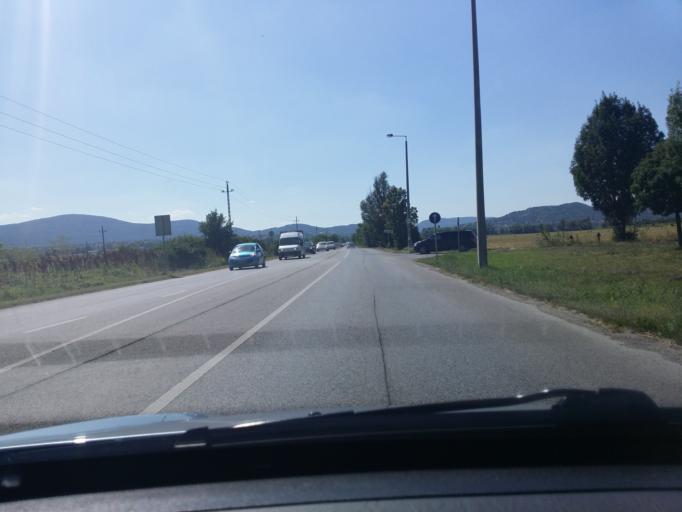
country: HU
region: Pest
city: Szentendre
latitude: 47.6456
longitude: 19.0631
